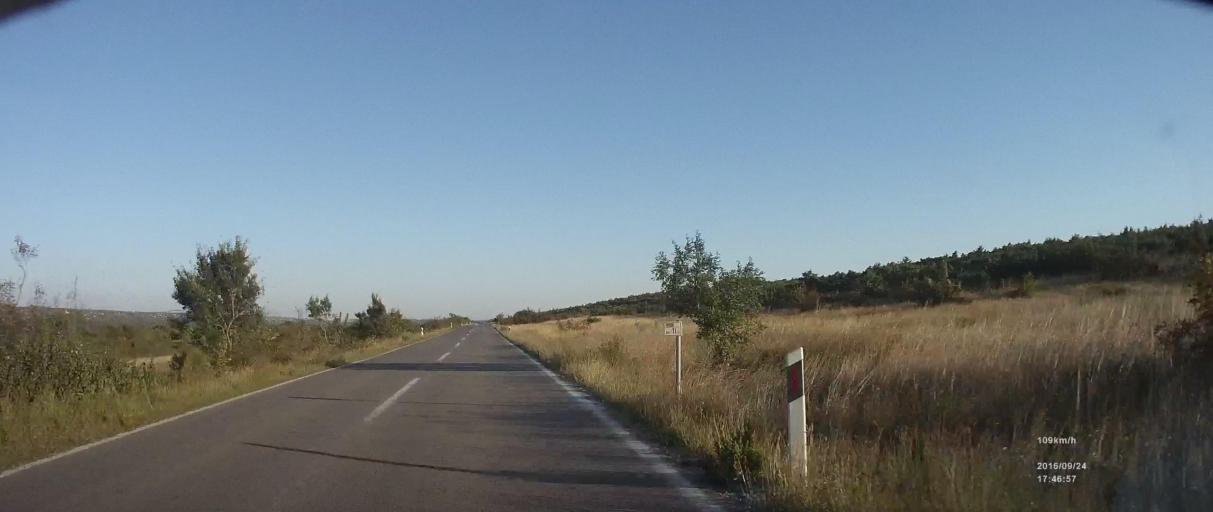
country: HR
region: Zadarska
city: Polaca
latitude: 44.0814
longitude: 15.5151
